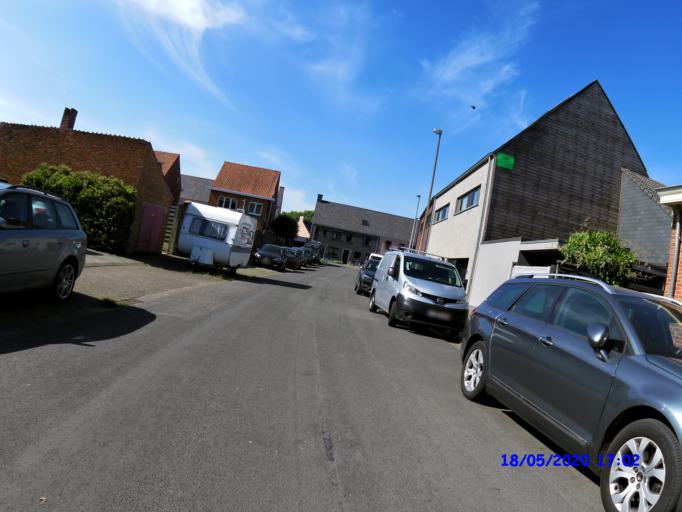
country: BE
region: Flanders
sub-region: Provincie Antwerpen
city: Herentals
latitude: 51.1823
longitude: 4.8231
